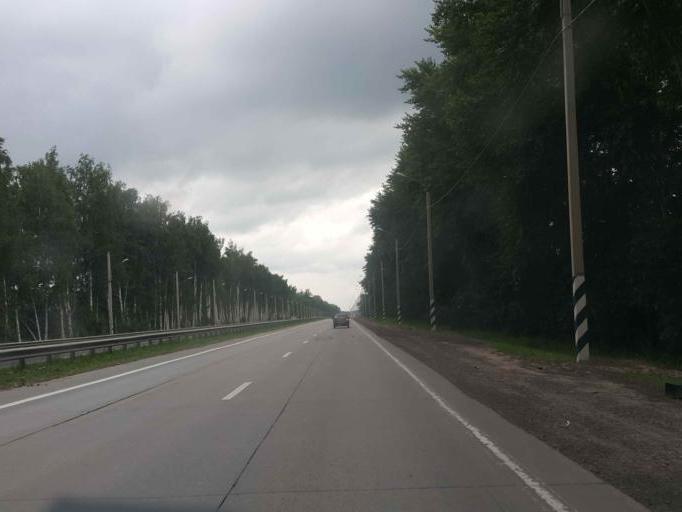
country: RU
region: Tambov
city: Selezni
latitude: 52.7555
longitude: 41.1600
